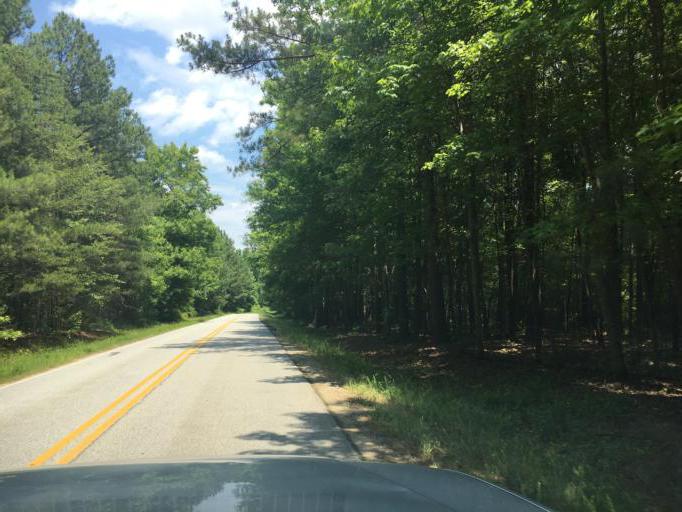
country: US
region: South Carolina
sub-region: Greenville County
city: Greer
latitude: 34.8955
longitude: -82.2061
